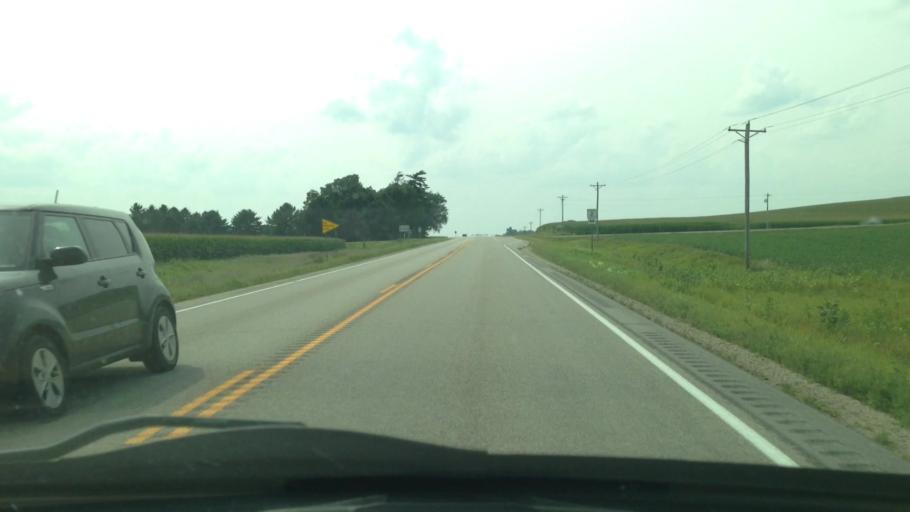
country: US
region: Minnesota
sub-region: Wabasha County
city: Elgin
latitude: 44.1654
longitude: -92.2569
